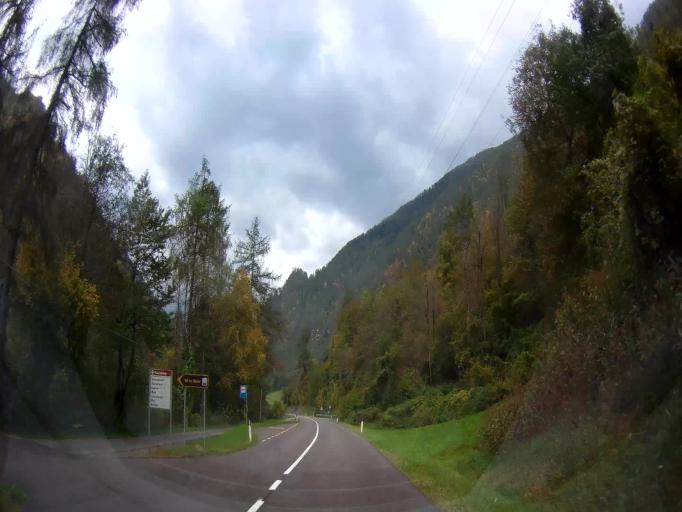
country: IT
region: Trentino-Alto Adige
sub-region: Bolzano
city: Certosa
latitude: 46.6783
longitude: 10.9372
